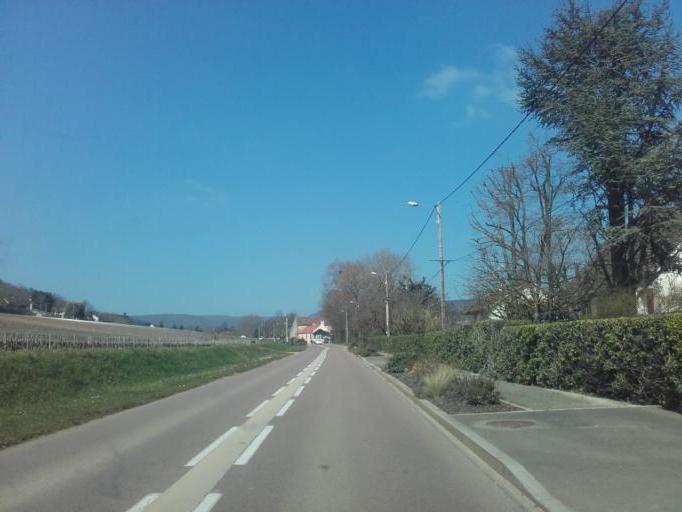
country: FR
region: Bourgogne
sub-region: Departement de la Cote-d'Or
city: Savigny-les-Beaune
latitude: 47.0567
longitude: 4.8334
